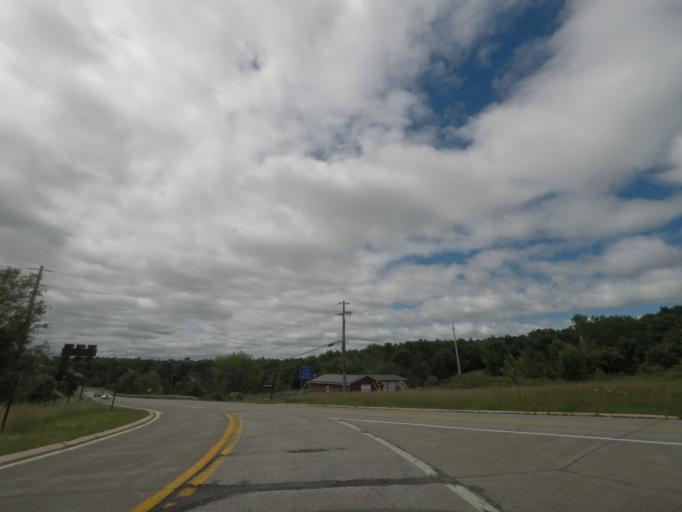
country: US
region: New York
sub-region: Columbia County
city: Philmont
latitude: 42.2573
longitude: -73.6158
